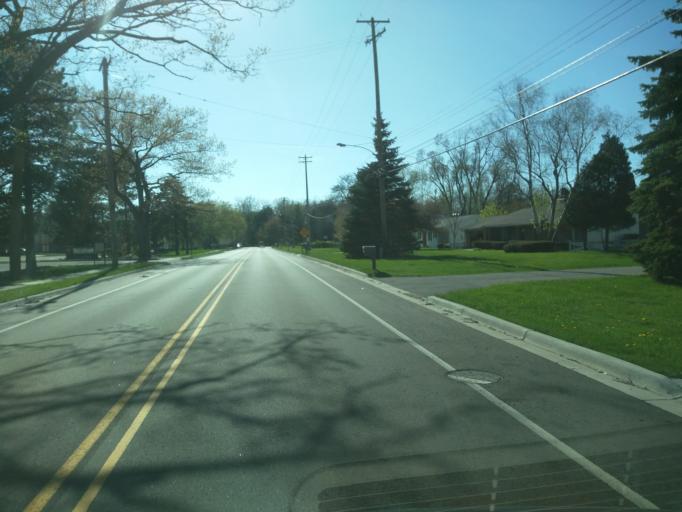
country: US
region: Michigan
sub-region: Eaton County
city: Waverly
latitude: 42.7483
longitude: -84.6102
